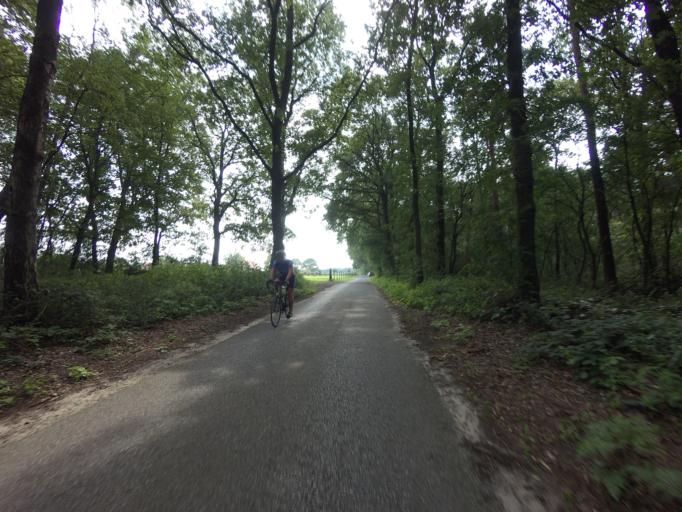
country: NL
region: Gelderland
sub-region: Gemeente Montferland
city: s-Heerenberg
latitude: 51.8804
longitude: 6.1790
